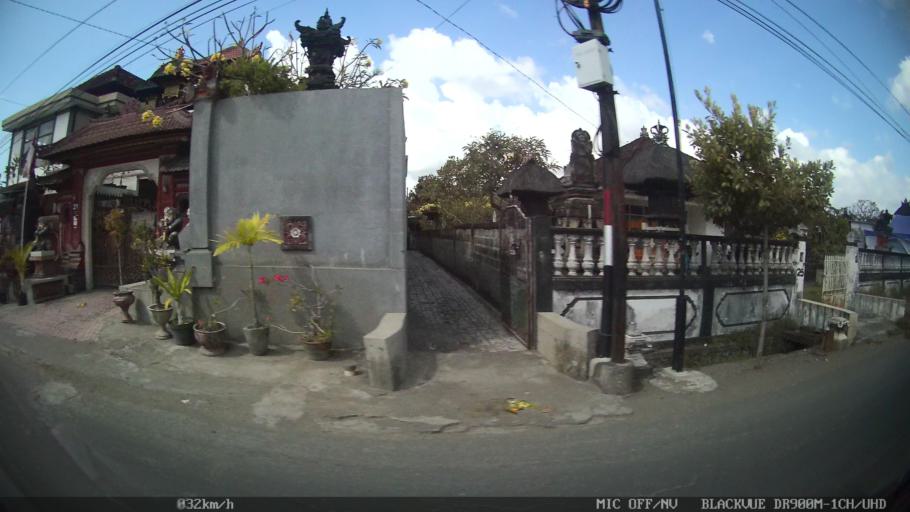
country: ID
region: Bali
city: Jabajero
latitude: -8.7188
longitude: 115.1972
